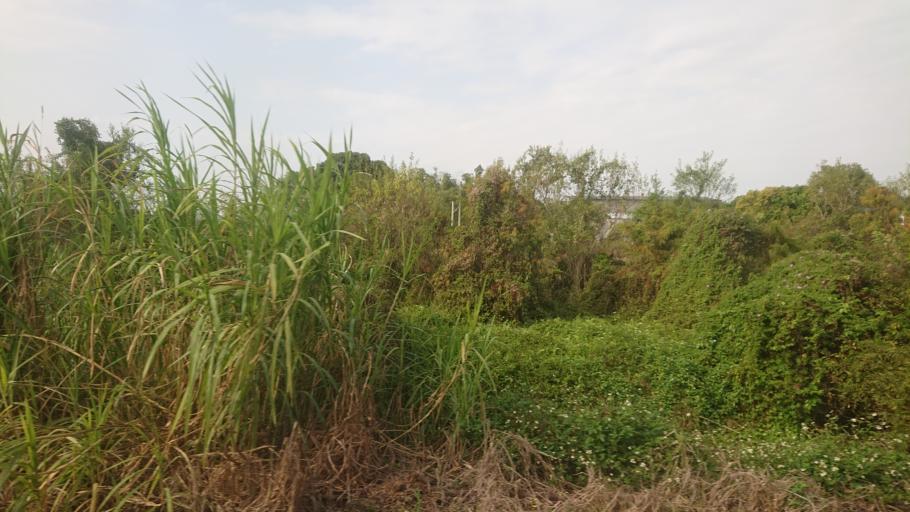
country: TW
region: Taiwan
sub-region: Nantou
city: Nantou
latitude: 23.8952
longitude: 120.5805
